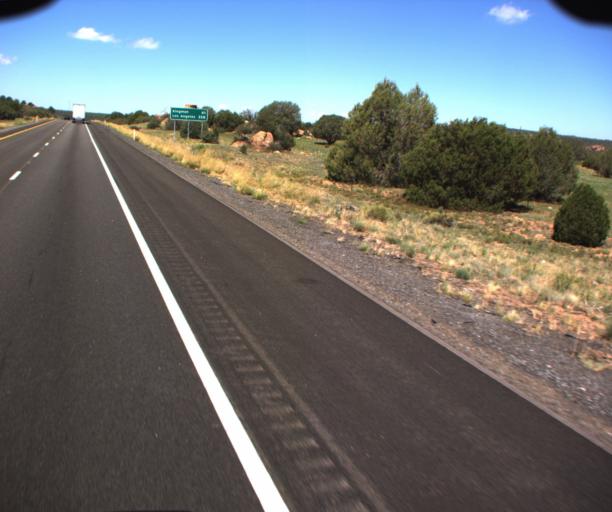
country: US
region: Arizona
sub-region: Mohave County
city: Peach Springs
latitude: 35.1909
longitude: -113.3794
